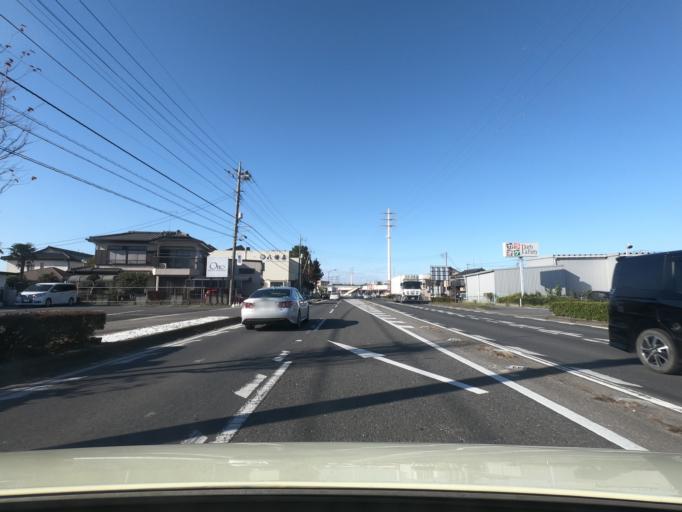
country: JP
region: Ibaraki
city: Ishige
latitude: 36.1826
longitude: 139.9503
